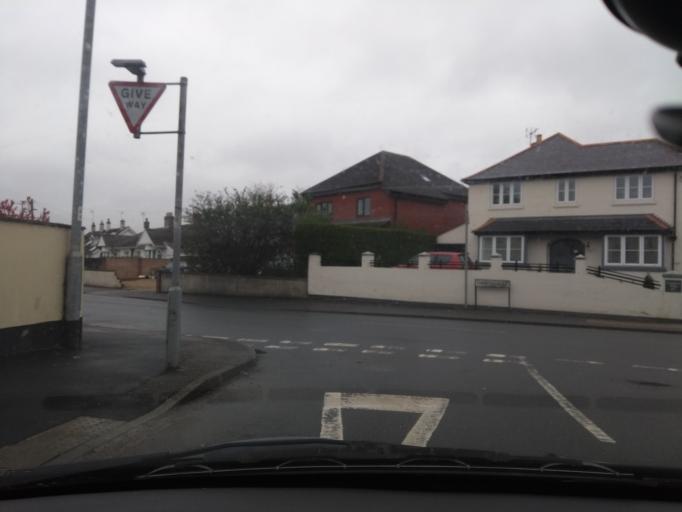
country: GB
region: England
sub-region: Somerset
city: Taunton
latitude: 51.0309
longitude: -3.1003
